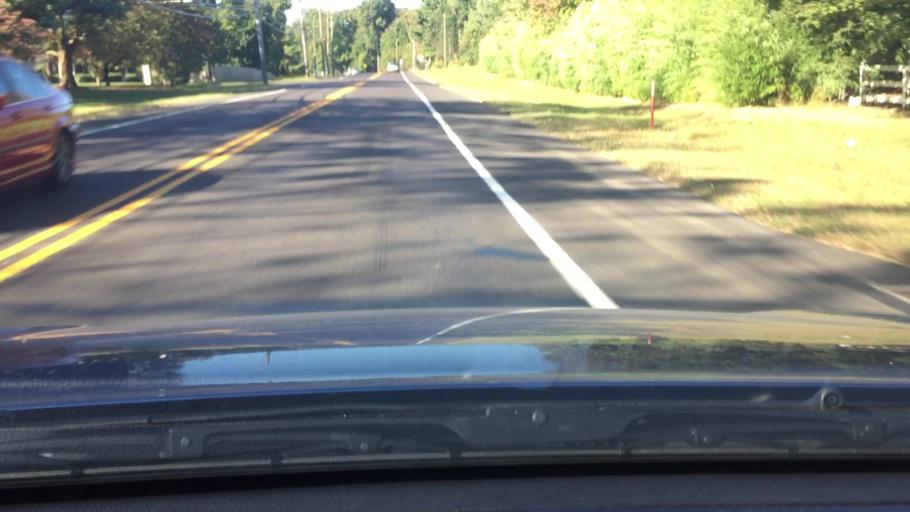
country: US
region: Pennsylvania
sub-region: Bucks County
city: Doylestown
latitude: 40.3163
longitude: -75.1003
